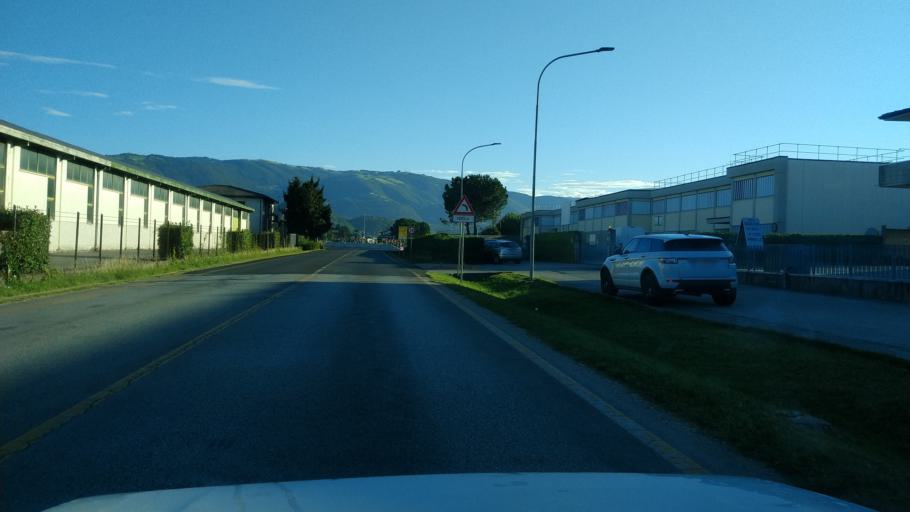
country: IT
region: Veneto
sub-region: Provincia di Vicenza
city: Marostica
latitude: 45.7253
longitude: 11.6516
